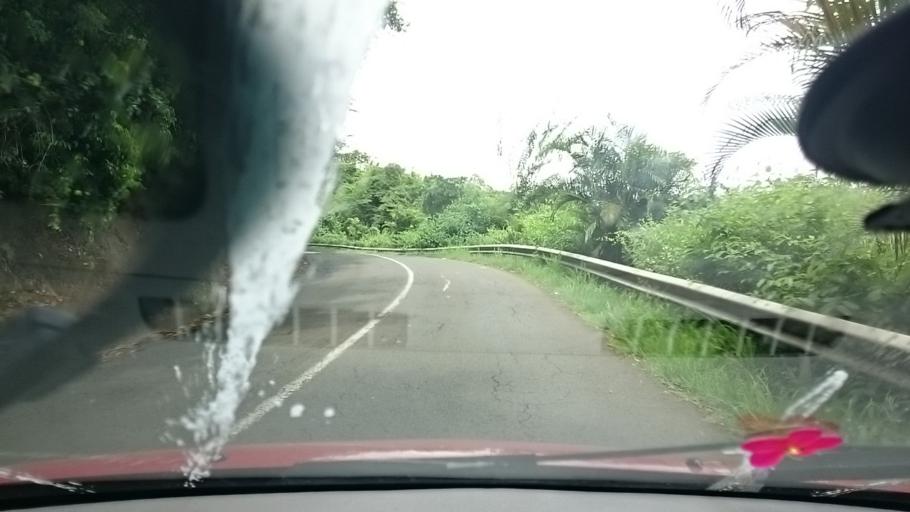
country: MQ
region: Martinique
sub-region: Martinique
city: La Trinite
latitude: 14.7561
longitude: -60.9222
